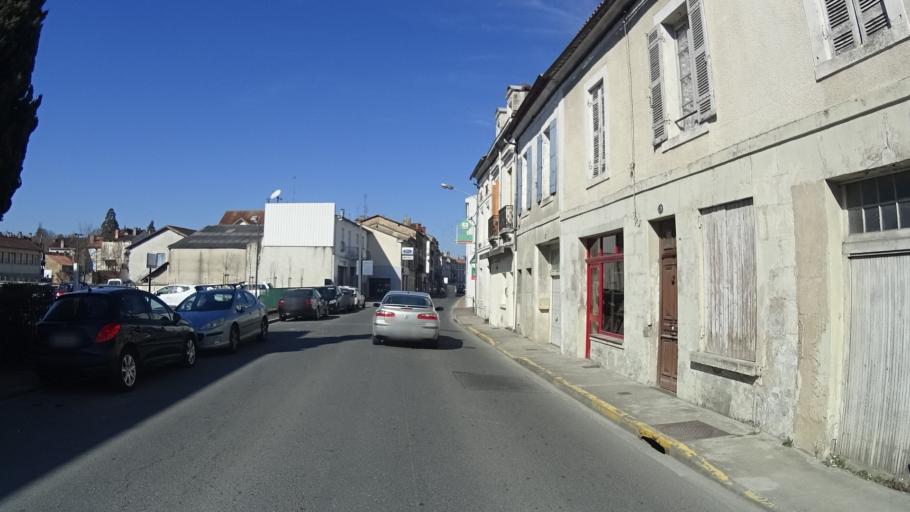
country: FR
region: Aquitaine
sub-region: Departement de la Dordogne
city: Riberac
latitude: 45.2457
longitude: 0.3410
